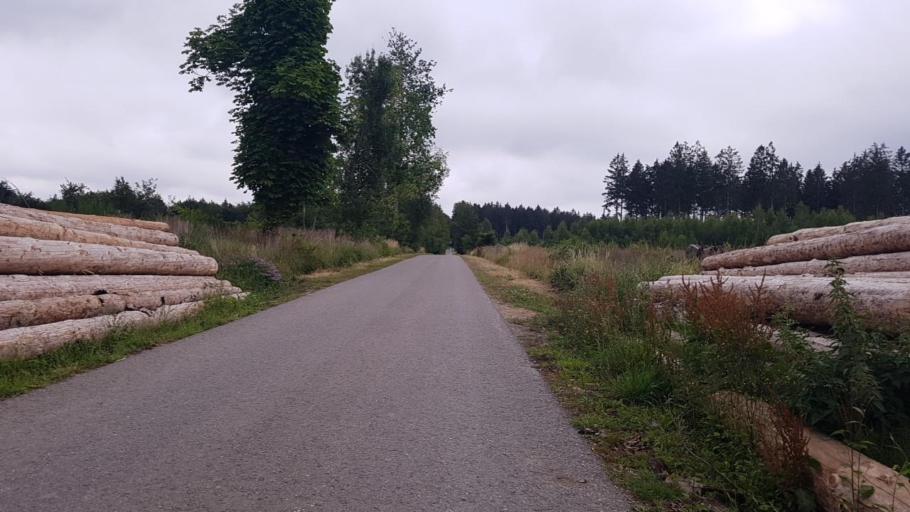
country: DE
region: North Rhine-Westphalia
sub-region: Regierungsbezirk Koln
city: Hurtgenwald
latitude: 50.7623
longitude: 6.3621
